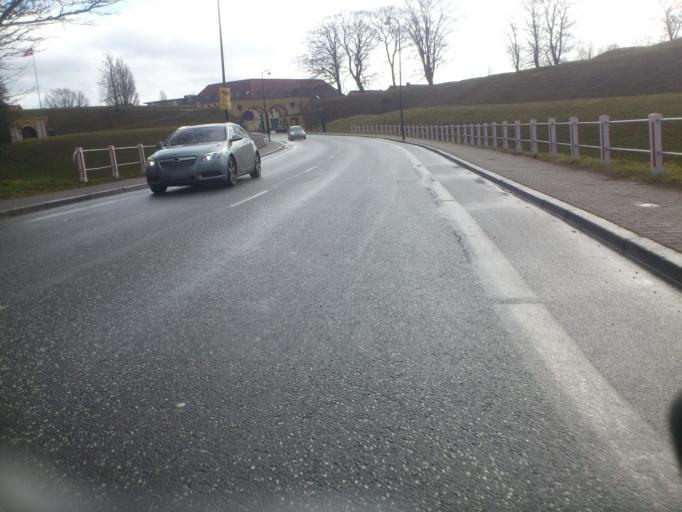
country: DK
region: South Denmark
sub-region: Fredericia Kommune
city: Fredericia
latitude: 55.5682
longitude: 9.7505
